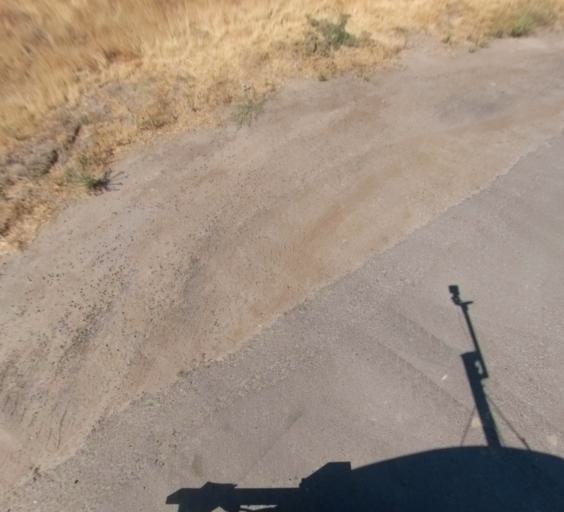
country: US
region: California
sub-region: Madera County
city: Bonadelle Ranchos-Madera Ranchos
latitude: 36.9885
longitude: -119.8669
